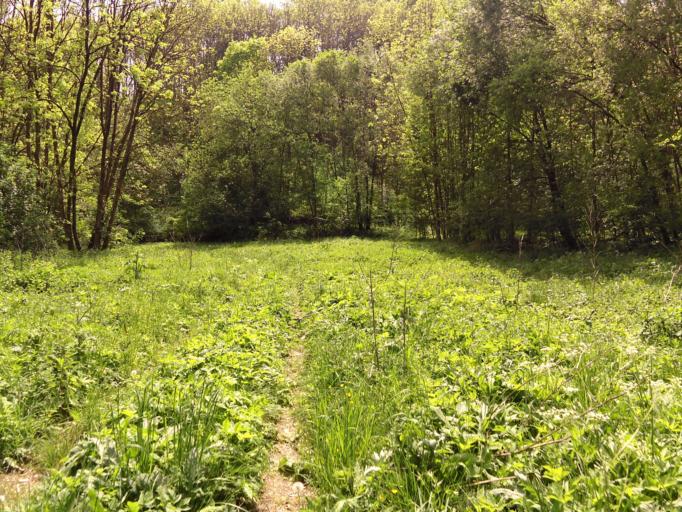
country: DE
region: Thuringia
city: Ifta
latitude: 51.0593
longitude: 10.1418
